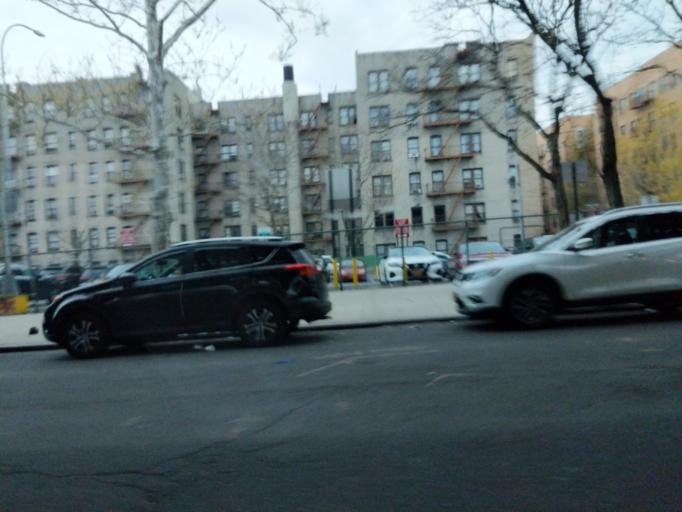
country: US
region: New York
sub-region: Bronx
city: The Bronx
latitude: 40.8534
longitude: -73.8677
